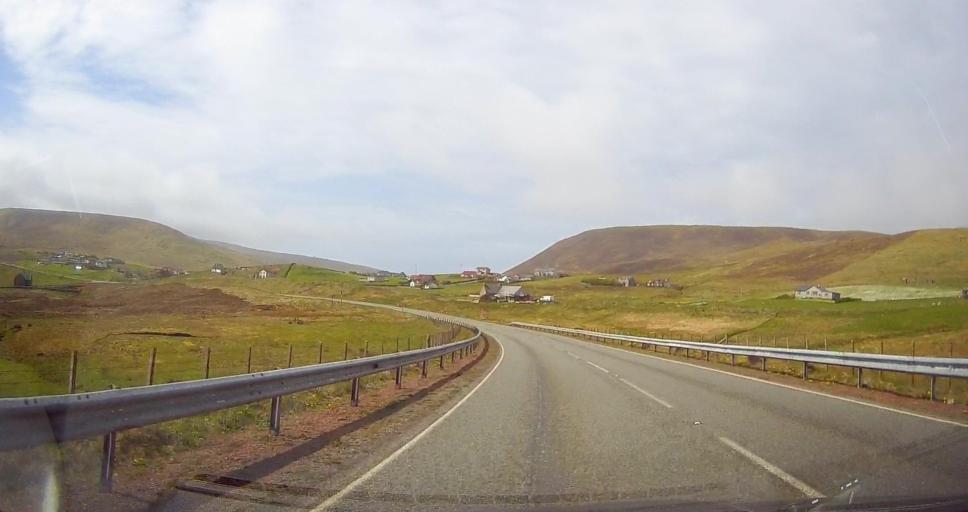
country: GB
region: Scotland
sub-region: Shetland Islands
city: Lerwick
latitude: 60.1045
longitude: -1.2270
